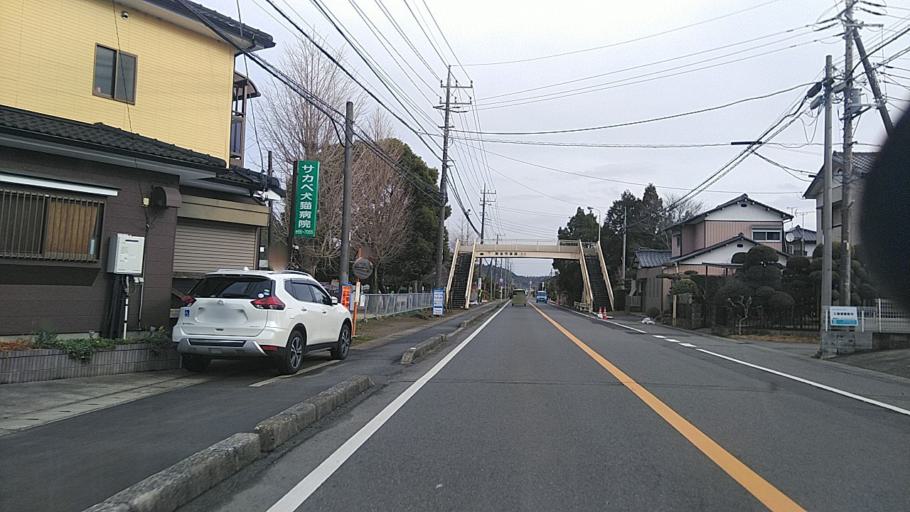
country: JP
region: Chiba
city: Togane
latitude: 35.5844
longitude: 140.3814
